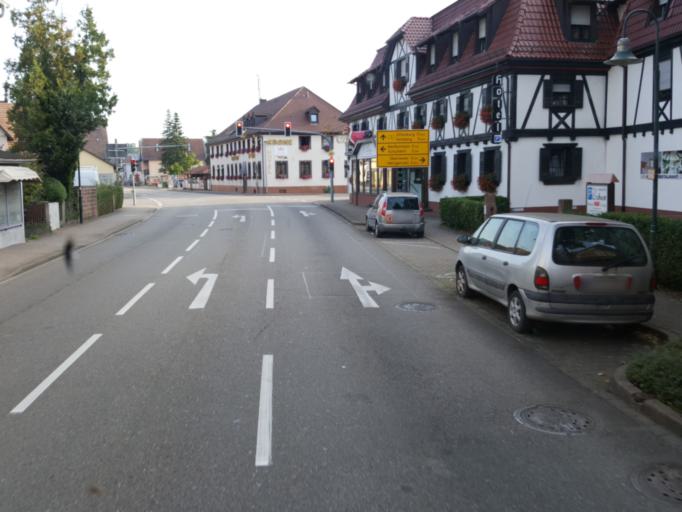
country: DE
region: Baden-Wuerttemberg
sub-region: Freiburg Region
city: Friesenheim
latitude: 48.3731
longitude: 7.8745
